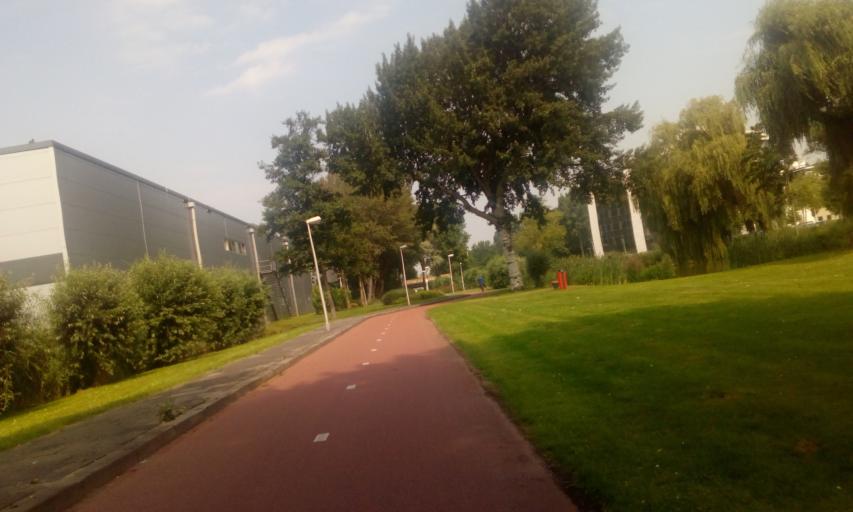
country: NL
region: South Holland
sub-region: Gemeente Capelle aan den IJssel
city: Capelle aan den IJssel
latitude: 51.9553
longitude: 4.5708
